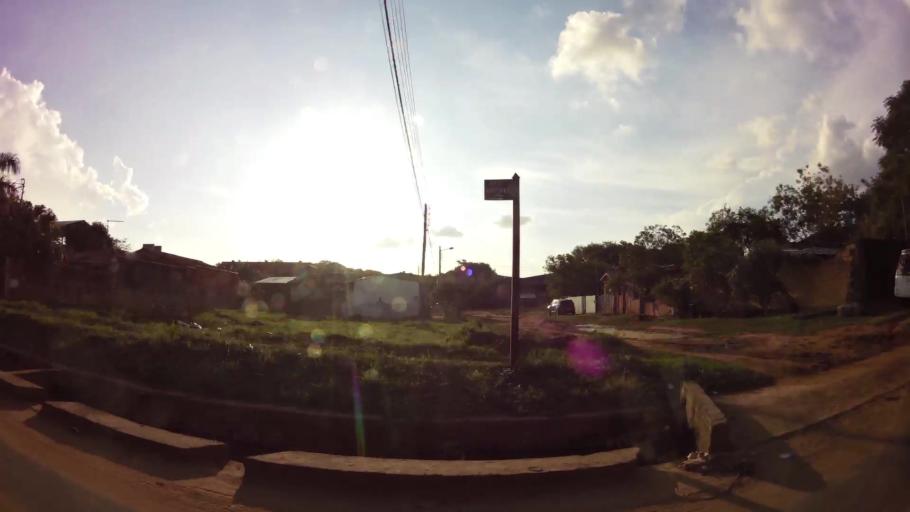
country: PY
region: Central
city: Fernando de la Mora
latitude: -25.3505
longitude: -57.5276
